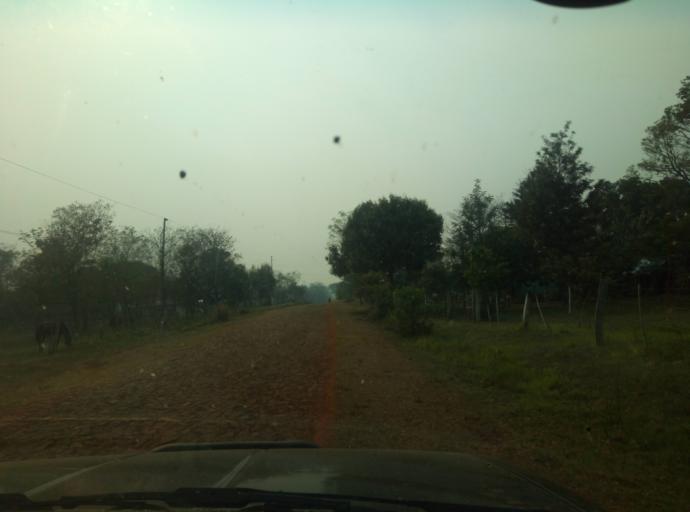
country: PY
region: Caaguazu
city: Carayao
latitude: -25.2041
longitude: -56.2450
